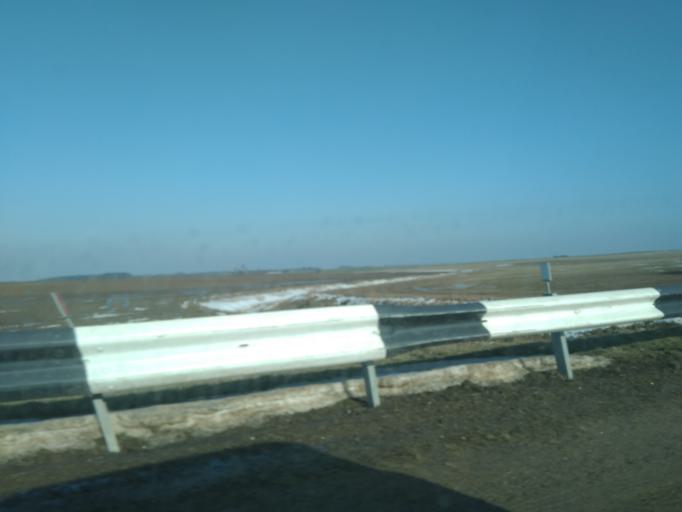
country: BY
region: Minsk
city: Snow
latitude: 53.2097
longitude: 26.4730
